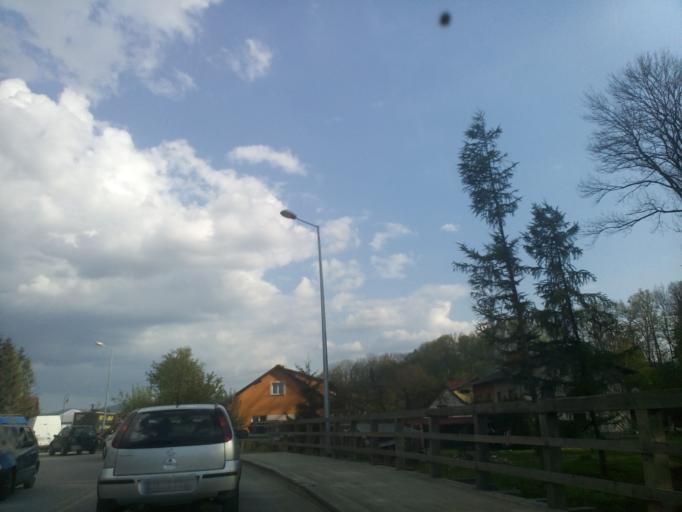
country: PL
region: Lesser Poland Voivodeship
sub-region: Powiat nowosadecki
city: Nawojowa
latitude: 49.5652
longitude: 20.7403
